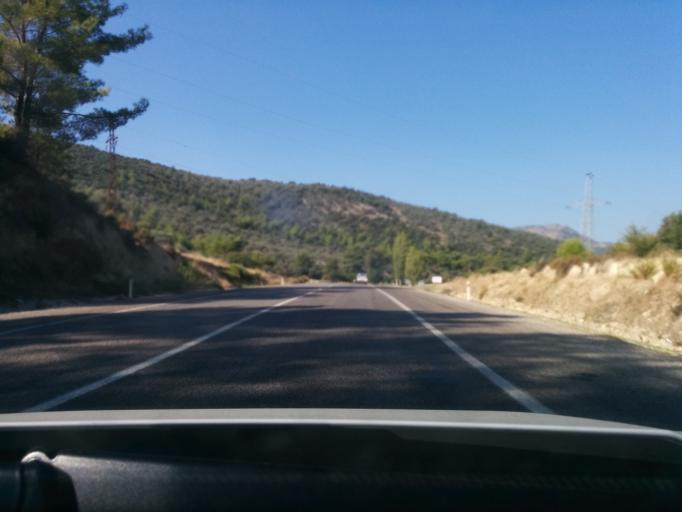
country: TR
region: Mugla
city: Esen
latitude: 36.4055
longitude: 29.2898
